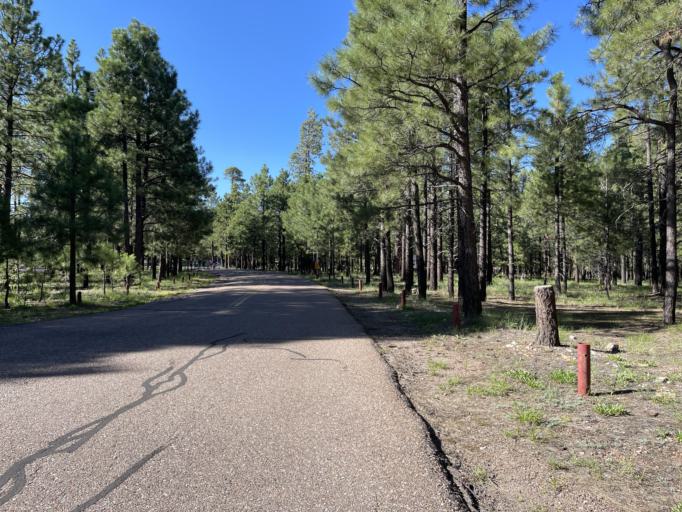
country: US
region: Arizona
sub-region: Navajo County
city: Heber-Overgaard
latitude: 34.3235
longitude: -110.8255
